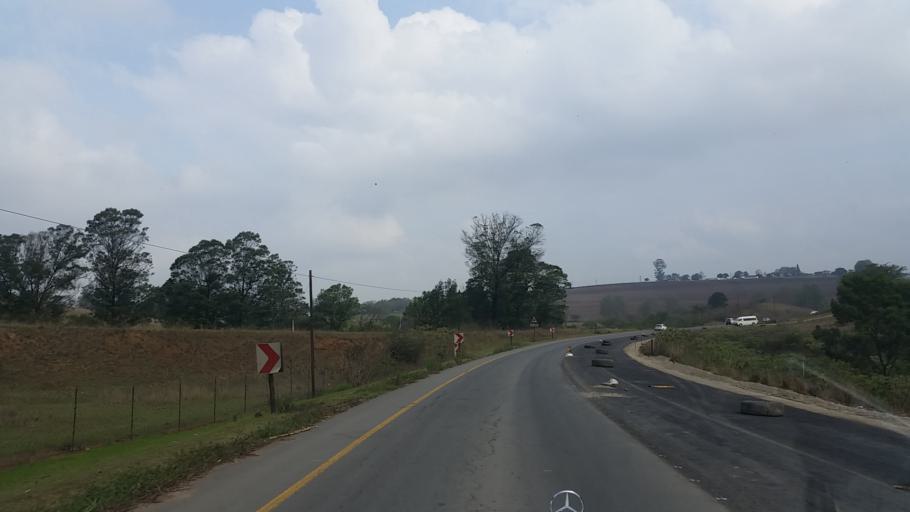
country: ZA
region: KwaZulu-Natal
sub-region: uMgungundlovu District Municipality
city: Camperdown
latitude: -29.7391
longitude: 30.5105
